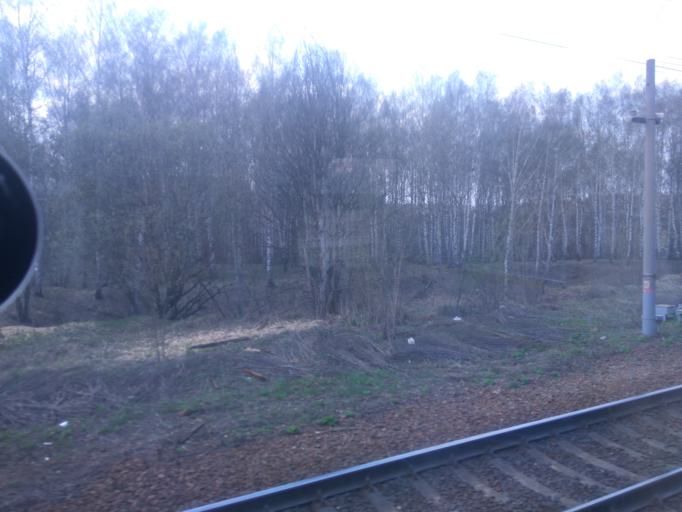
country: RU
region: Moskovskaya
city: Yakhroma
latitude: 56.2938
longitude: 37.4974
